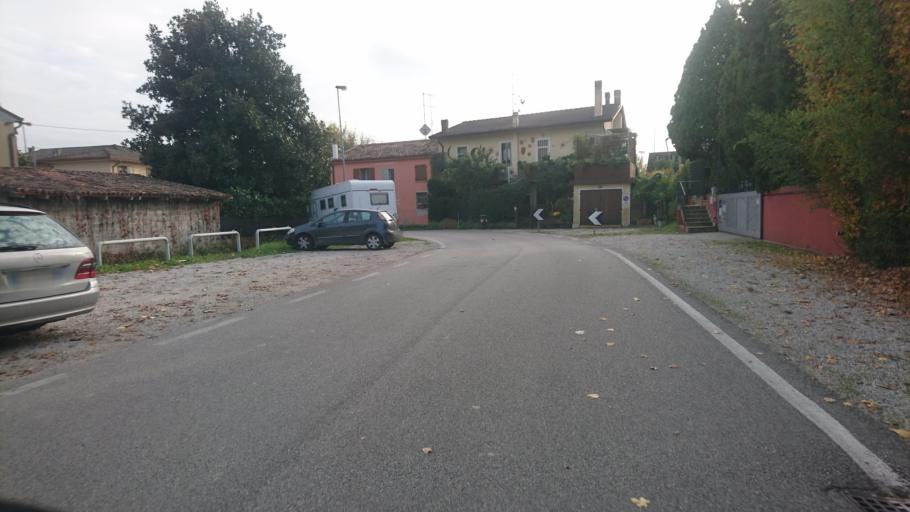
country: IT
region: Veneto
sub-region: Provincia di Padova
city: Mandriola-Sant'Agostino
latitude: 45.3829
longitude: 11.8361
